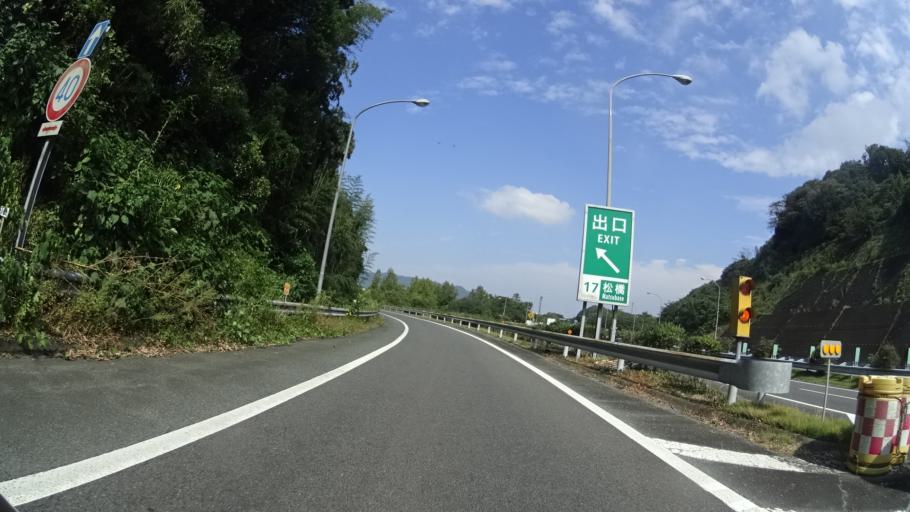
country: JP
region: Kumamoto
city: Matsubase
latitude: 32.6461
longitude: 130.7070
